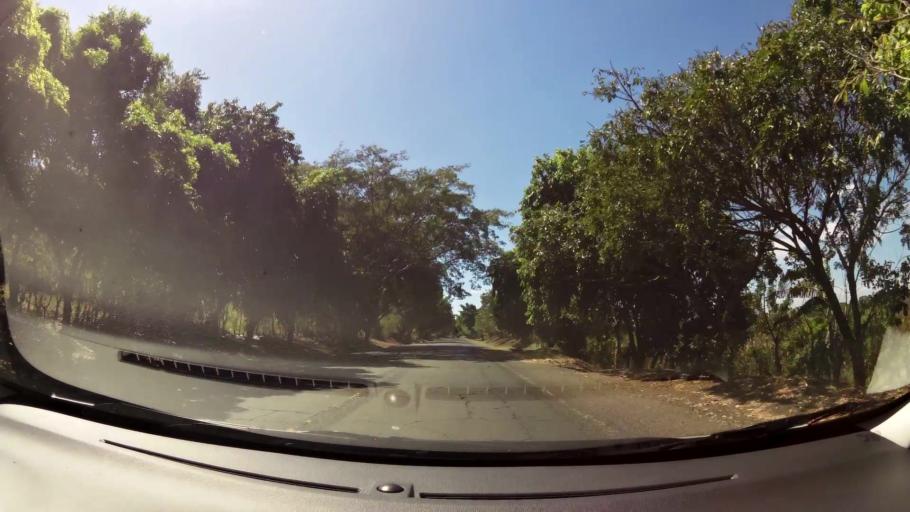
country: SV
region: Ahuachapan
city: Ahuachapan
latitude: 13.9523
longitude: -89.8352
